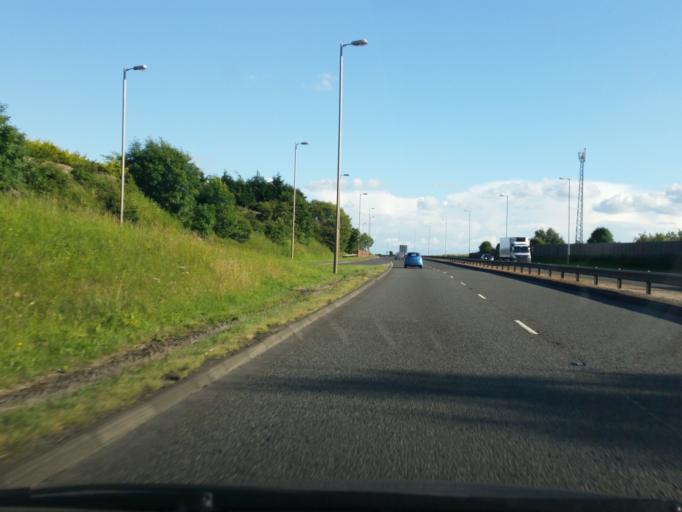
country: GB
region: Scotland
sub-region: North Lanarkshire
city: Bellshill
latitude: 55.8194
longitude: -4.0395
